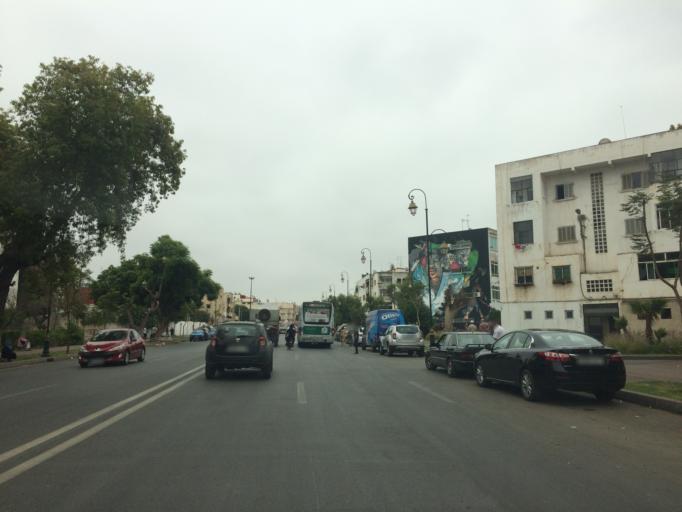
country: MA
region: Rabat-Sale-Zemmour-Zaer
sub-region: Rabat
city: Rabat
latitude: 33.9953
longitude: -6.8200
